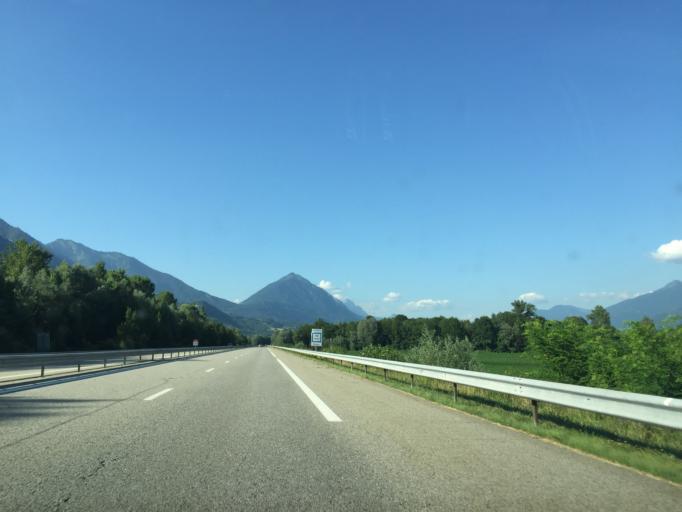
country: FR
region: Rhone-Alpes
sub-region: Departement de la Savoie
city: Gresy-sur-Isere
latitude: 45.5918
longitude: 6.2763
